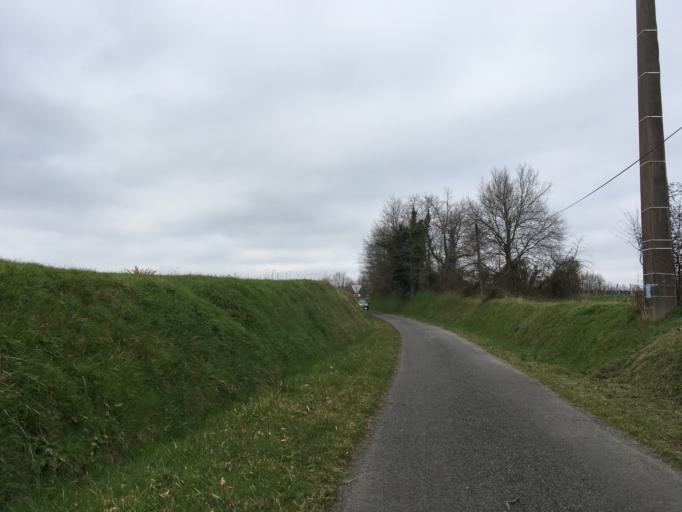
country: FR
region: Aquitaine
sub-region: Departement de la Gironde
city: Saint-Ciers-sur-Gironde
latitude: 45.3145
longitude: -0.5893
